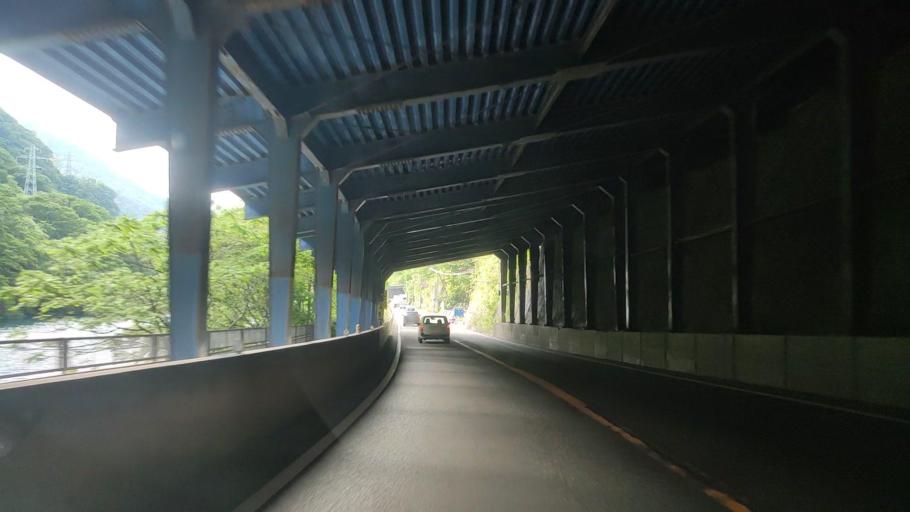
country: JP
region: Toyama
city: Yatsuomachi-higashikumisaka
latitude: 36.4218
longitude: 137.2858
